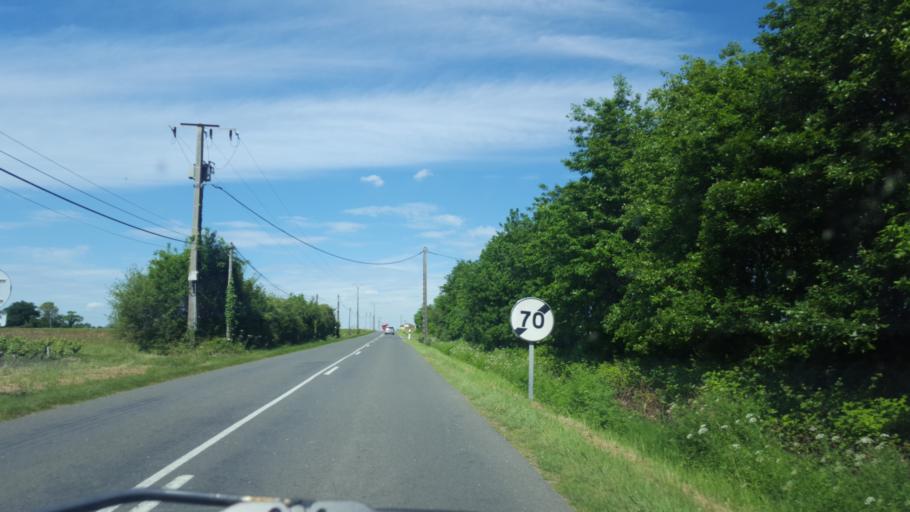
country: FR
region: Pays de la Loire
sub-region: Departement de la Loire-Atlantique
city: Saint-Philbert-de-Grand-Lieu
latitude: 47.0090
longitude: -1.6541
